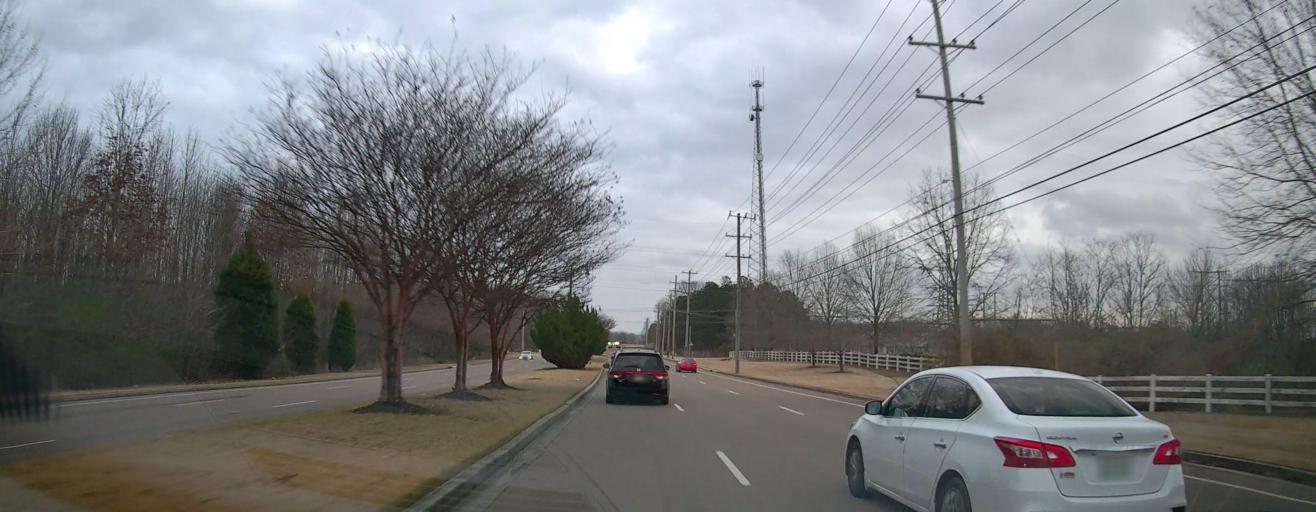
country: US
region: Tennessee
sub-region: Shelby County
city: Germantown
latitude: 35.0471
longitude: -89.7441
